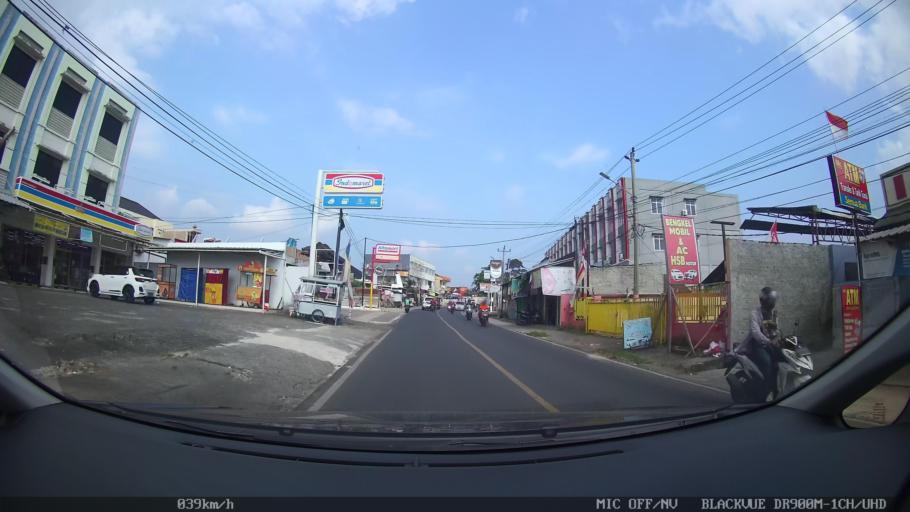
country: ID
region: Lampung
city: Kedaton
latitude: -5.3948
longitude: 105.2352
